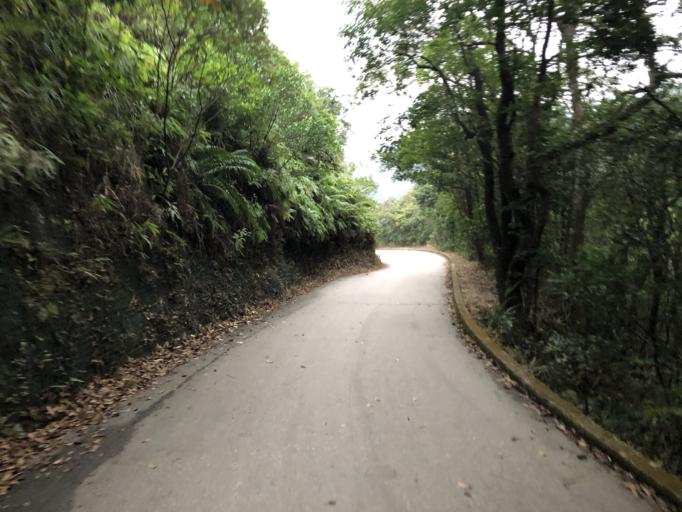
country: HK
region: Wanchai
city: Wan Chai
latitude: 22.2614
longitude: 114.2140
